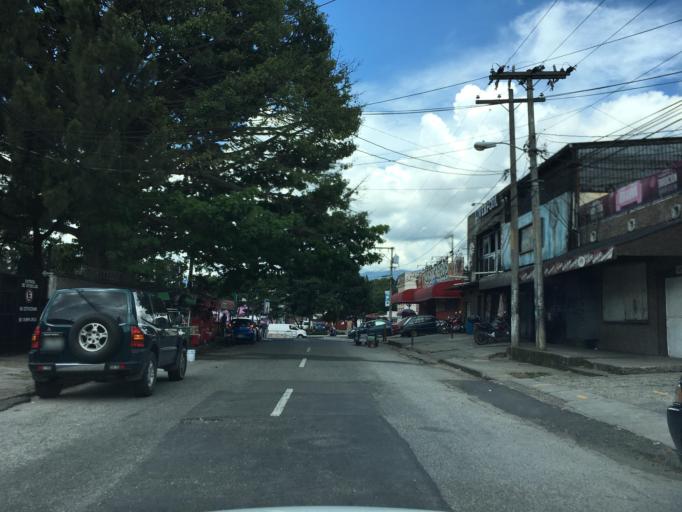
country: GT
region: Guatemala
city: Santa Catarina Pinula
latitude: 14.5901
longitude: -90.5506
